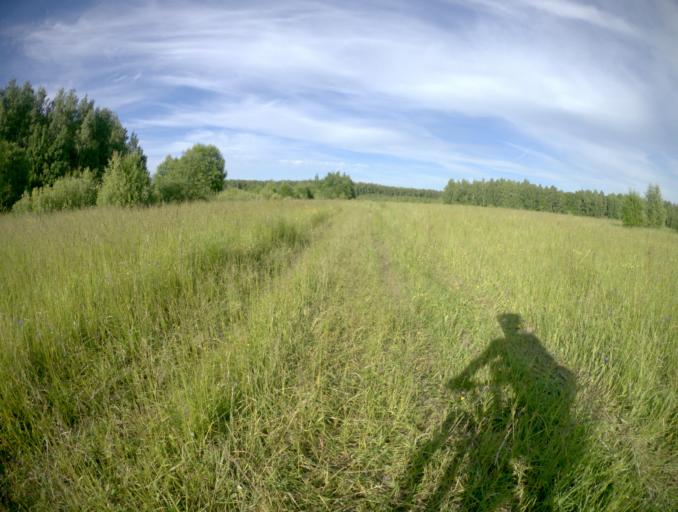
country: RU
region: Vladimir
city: Vorsha
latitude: 56.1696
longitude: 40.2122
